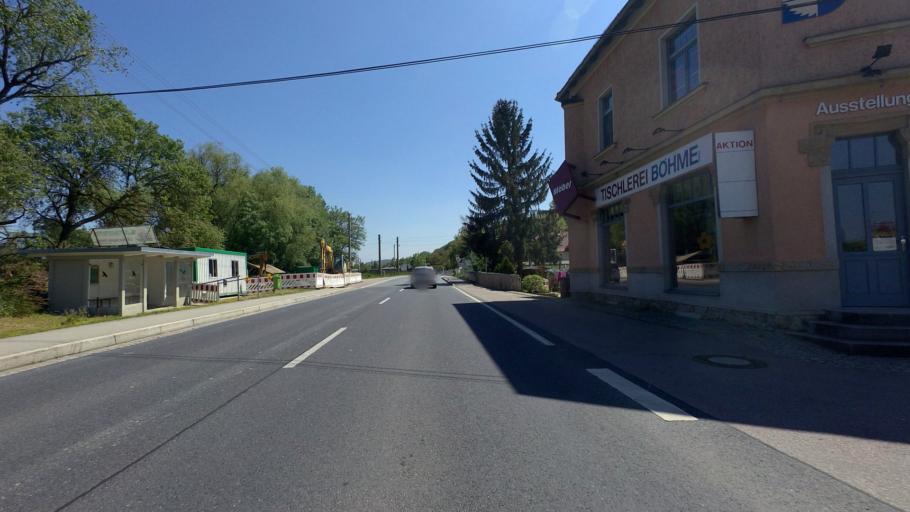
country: DE
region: Saxony
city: Coswig
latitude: 51.1105
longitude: 13.5688
